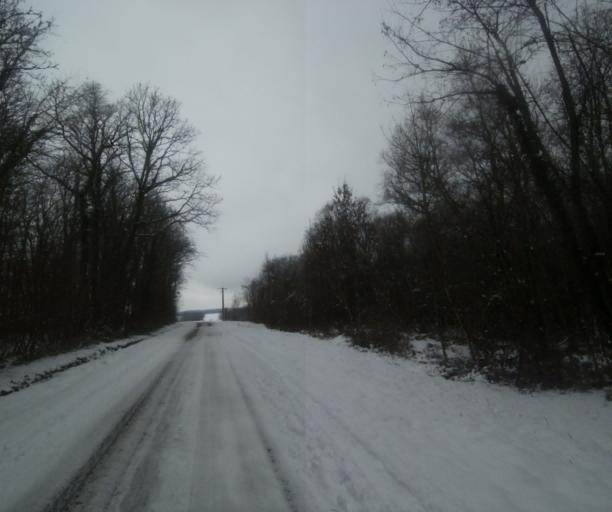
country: FR
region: Champagne-Ardenne
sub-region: Departement de la Haute-Marne
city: Laneuville-a-Remy
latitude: 48.5112
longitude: 4.8918
